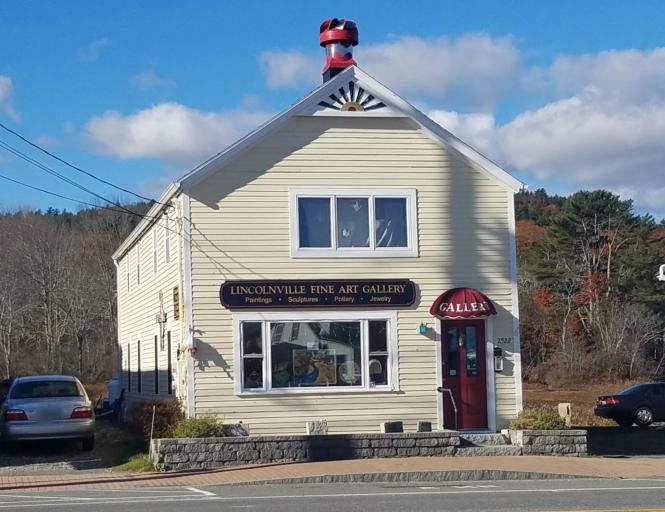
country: US
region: Maine
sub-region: Waldo County
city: Lincolnville
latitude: 44.2828
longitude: -69.0084
